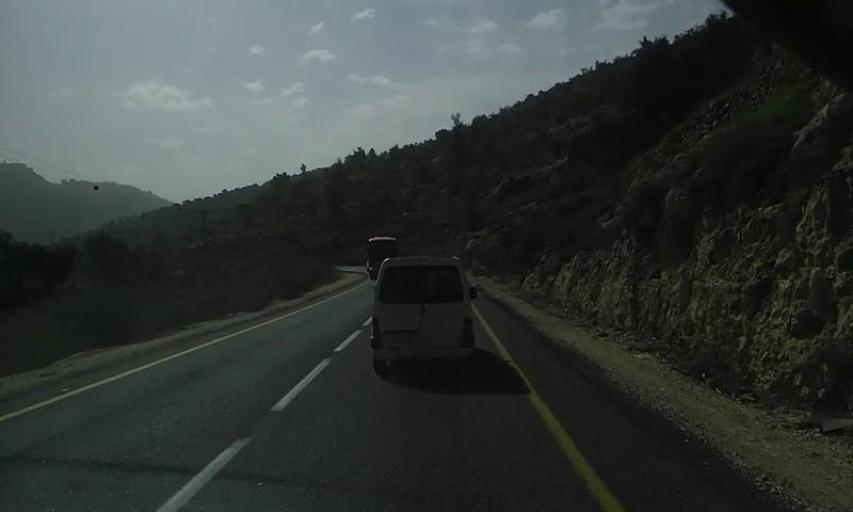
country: PS
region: West Bank
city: Silwad
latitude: 31.9959
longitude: 35.2414
